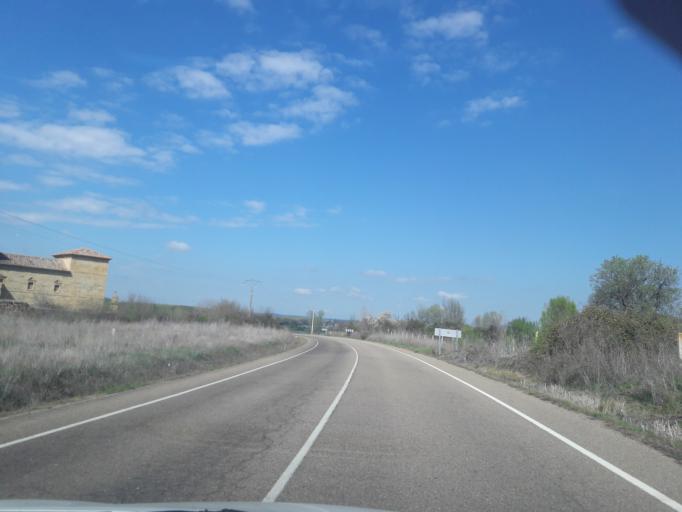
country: ES
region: Castille and Leon
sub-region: Provincia de Salamanca
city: Ciudad Rodrigo
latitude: 40.5740
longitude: -6.4928
